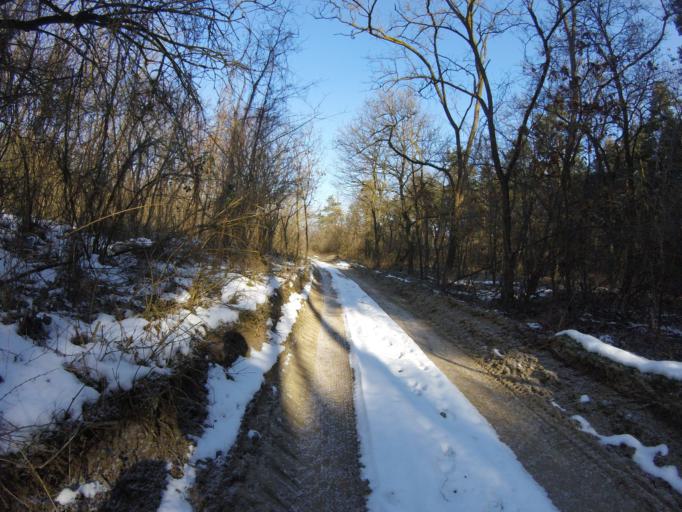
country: HU
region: Komarom-Esztergom
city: Piliscsev
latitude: 47.6664
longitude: 18.8283
